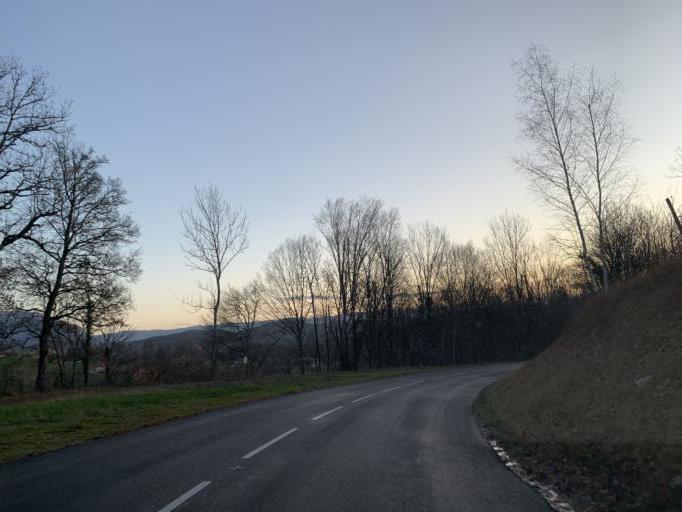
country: FR
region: Rhone-Alpes
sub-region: Departement de l'Ain
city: Belley
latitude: 45.7888
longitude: 5.6488
